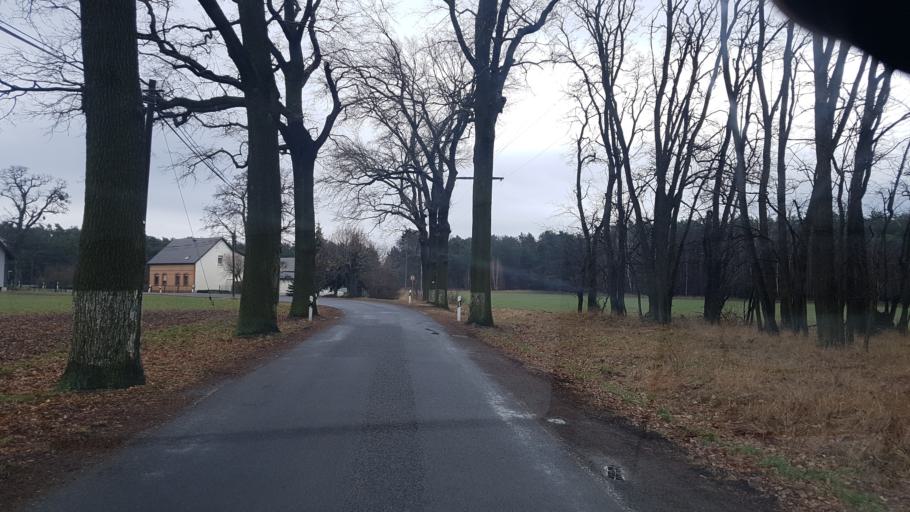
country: DE
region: Brandenburg
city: Neupetershain
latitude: 51.6181
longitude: 14.1079
